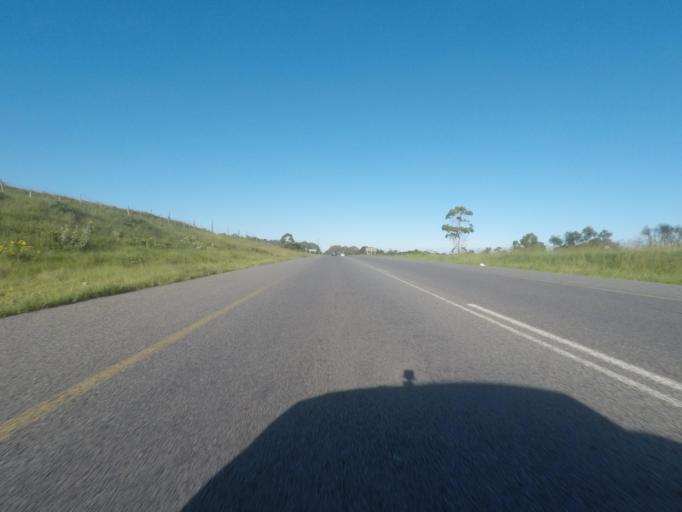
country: ZA
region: Eastern Cape
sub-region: Buffalo City Metropolitan Municipality
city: East London
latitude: -33.0493
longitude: 27.8167
